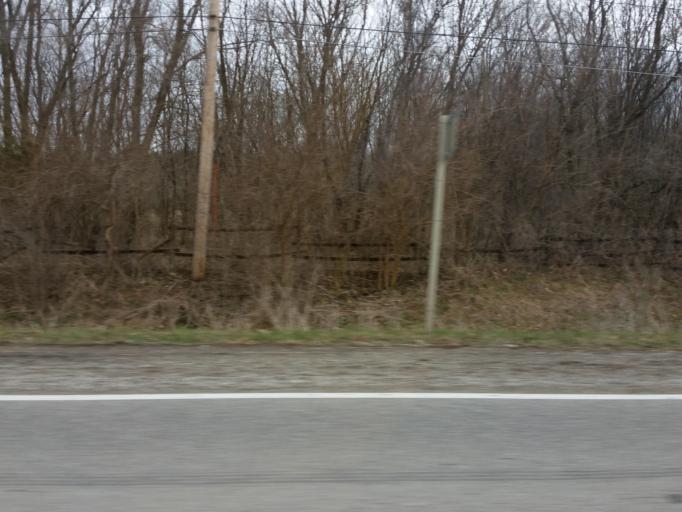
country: US
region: Iowa
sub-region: Black Hawk County
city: Elk Run Heights
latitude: 42.4620
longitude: -92.2198
